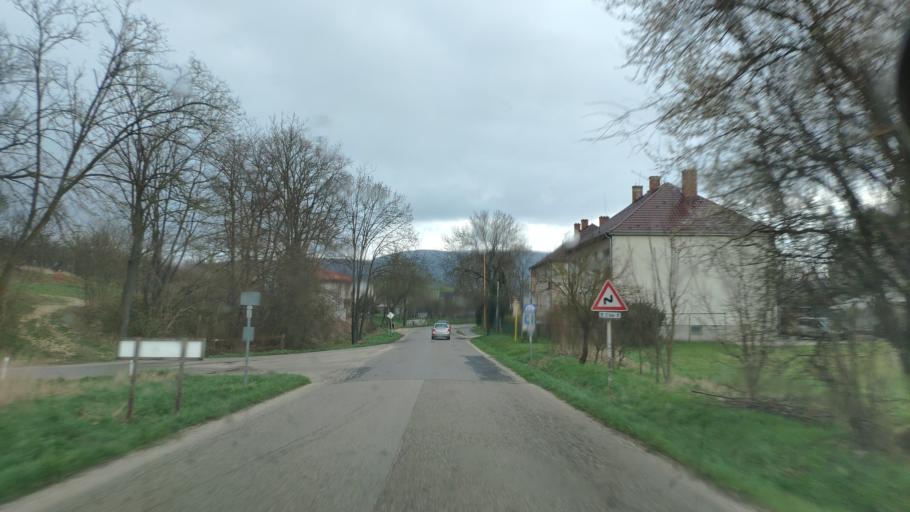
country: SK
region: Nitriansky
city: Stara Tura
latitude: 48.7906
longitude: 17.7330
